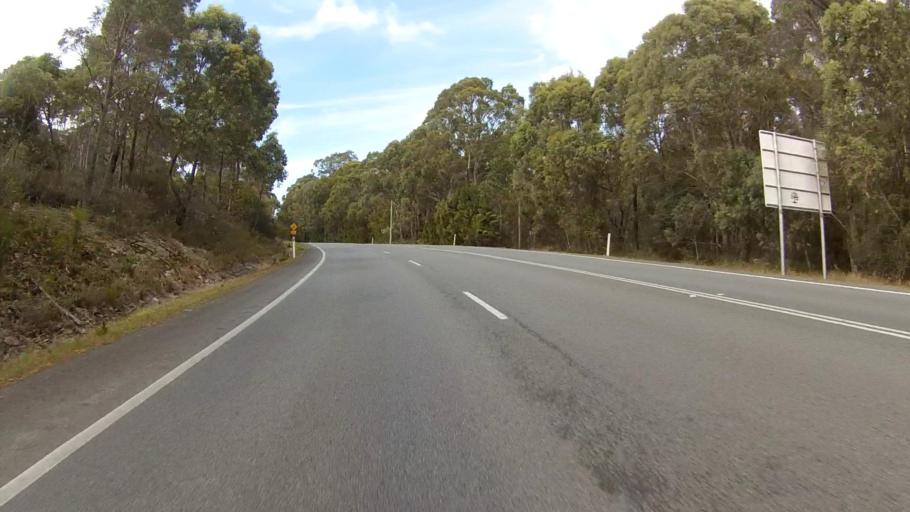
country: AU
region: Tasmania
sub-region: Kingborough
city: Kettering
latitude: -43.1090
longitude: 147.2425
